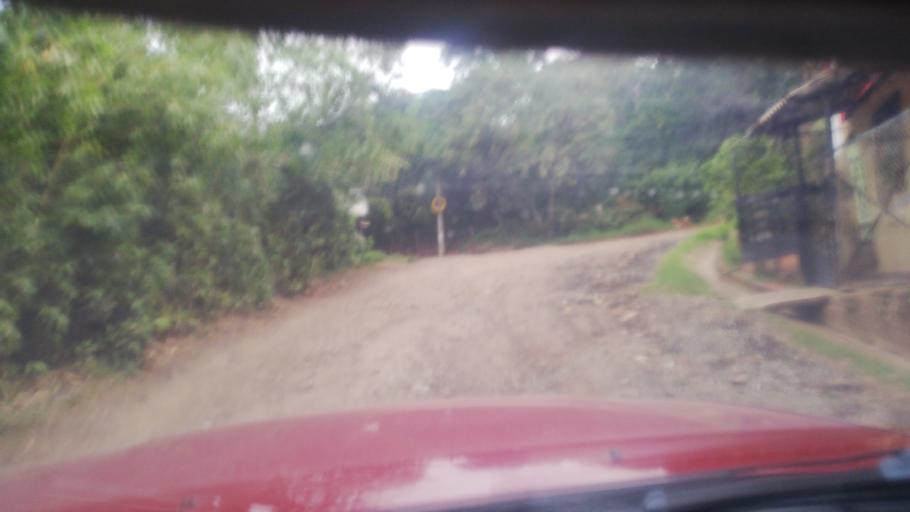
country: CO
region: Valle del Cauca
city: Cali
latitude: 3.5005
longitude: -76.5486
